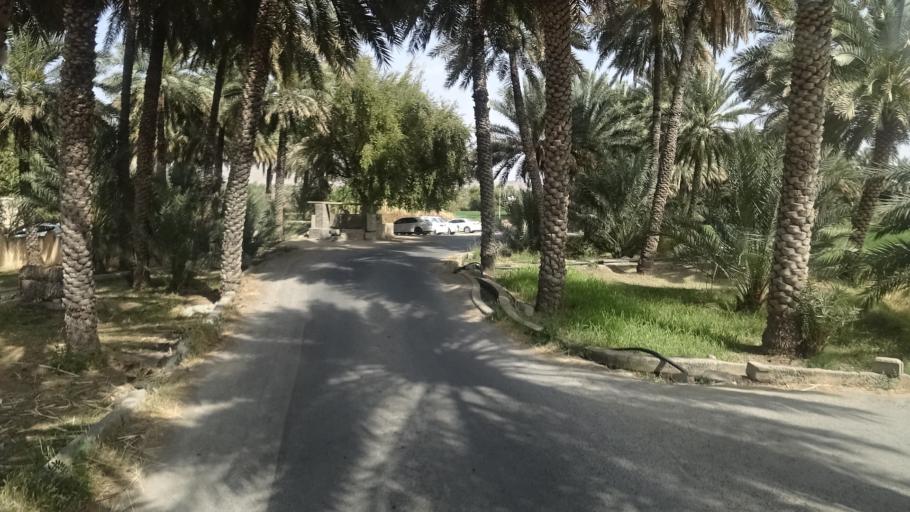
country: OM
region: Muhafazat ad Dakhiliyah
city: Bahla'
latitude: 23.0970
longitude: 57.3080
